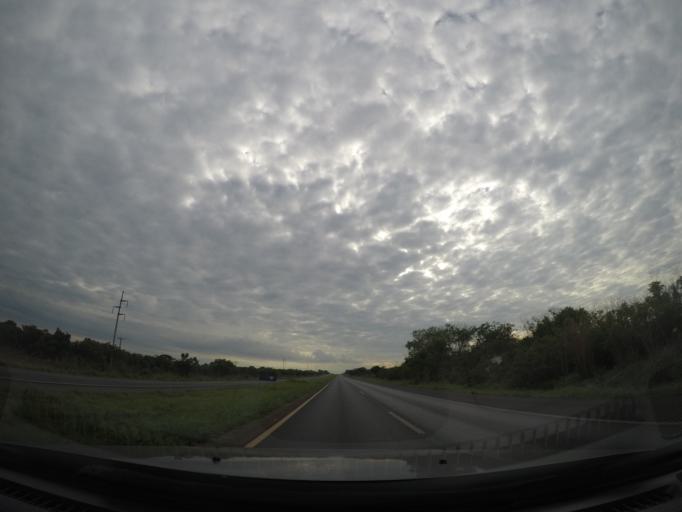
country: BR
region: Goias
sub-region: Planaltina
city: Planaltina
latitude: -15.5959
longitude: -47.6463
